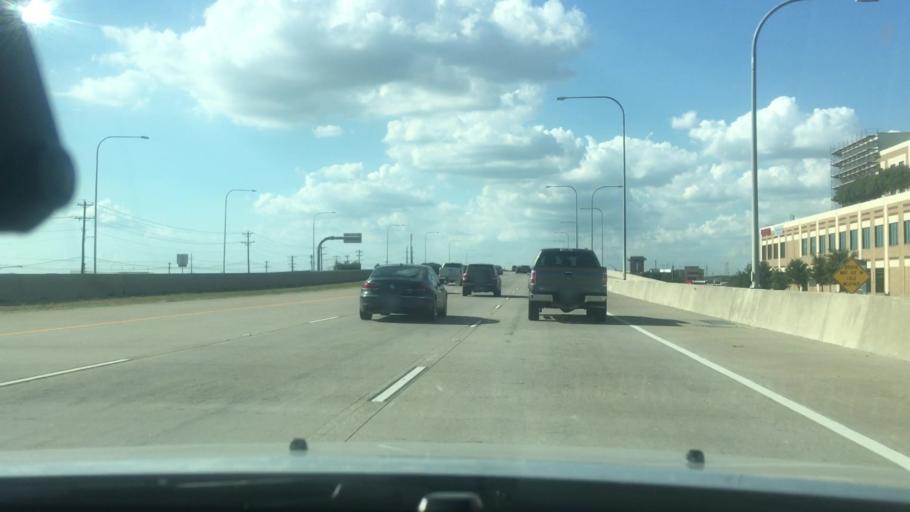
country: US
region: Texas
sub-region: Collin County
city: Frisco
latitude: 33.1496
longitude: -96.8396
